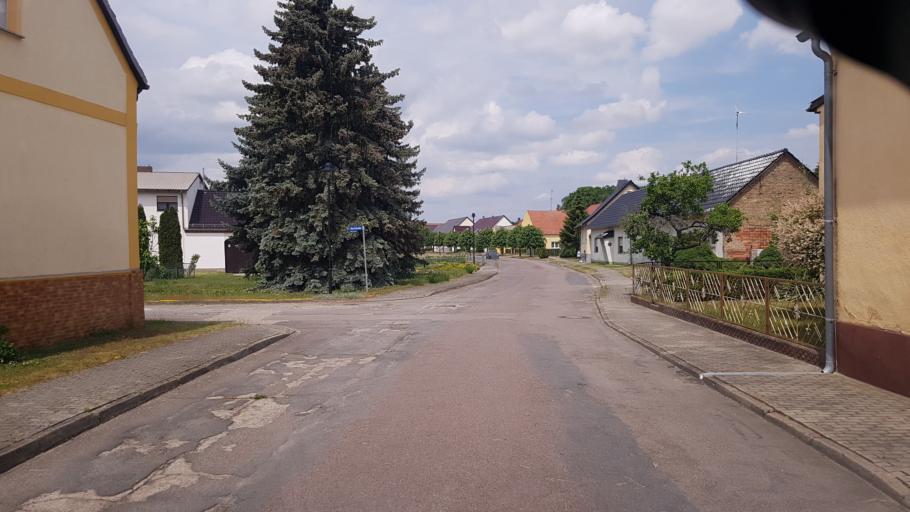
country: DE
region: Brandenburg
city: Ihlow
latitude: 51.8603
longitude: 13.2969
